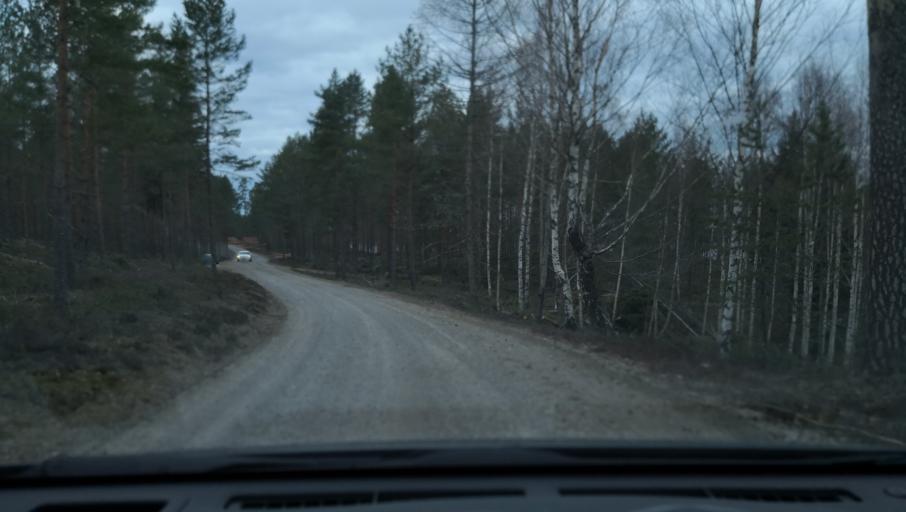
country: SE
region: Soedermanland
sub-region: Katrineholms Kommun
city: Katrineholm
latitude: 59.1340
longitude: 16.1465
